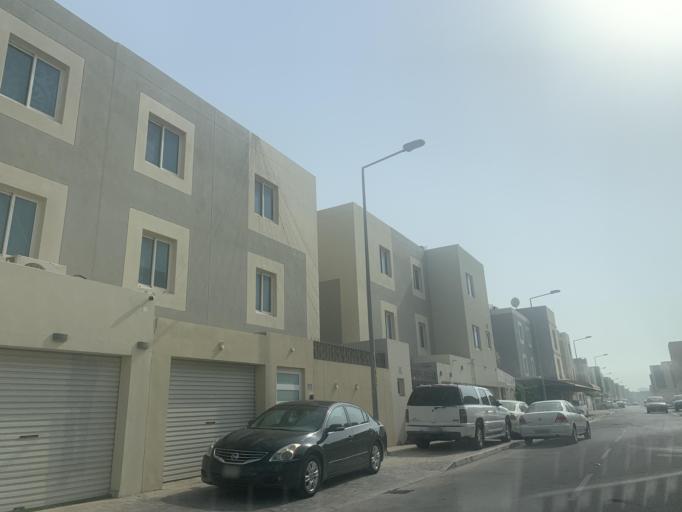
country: BH
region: Manama
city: Jidd Hafs
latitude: 26.2319
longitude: 50.4484
